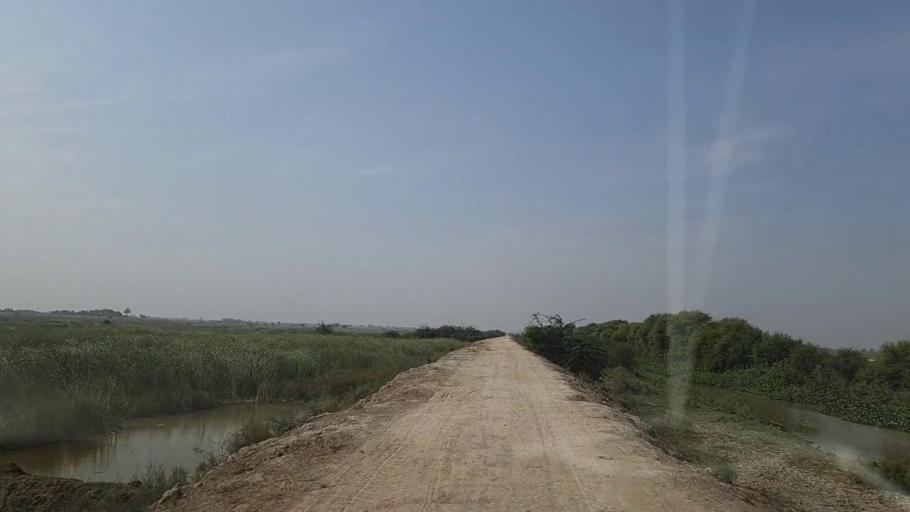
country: PK
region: Sindh
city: Mirpur Batoro
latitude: 24.6543
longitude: 68.2432
